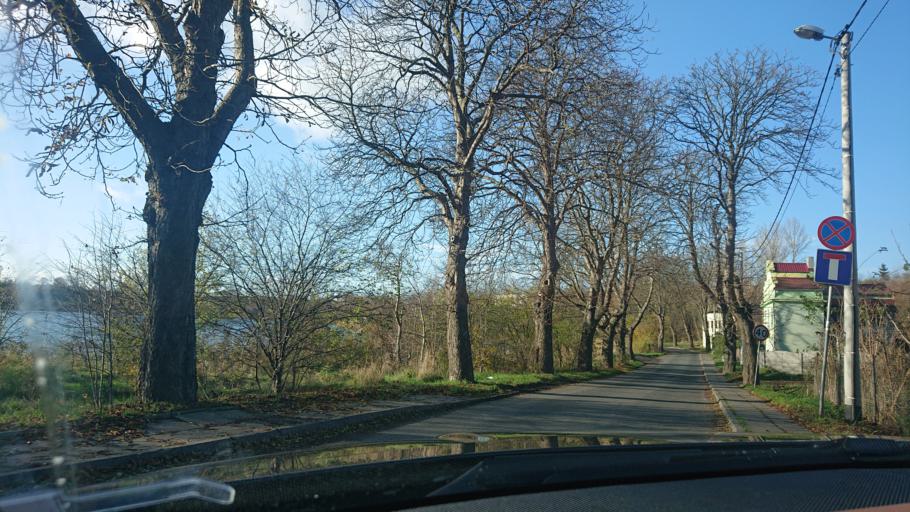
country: PL
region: Greater Poland Voivodeship
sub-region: Powiat gnieznienski
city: Gniezno
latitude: 52.5448
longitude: 17.6004
